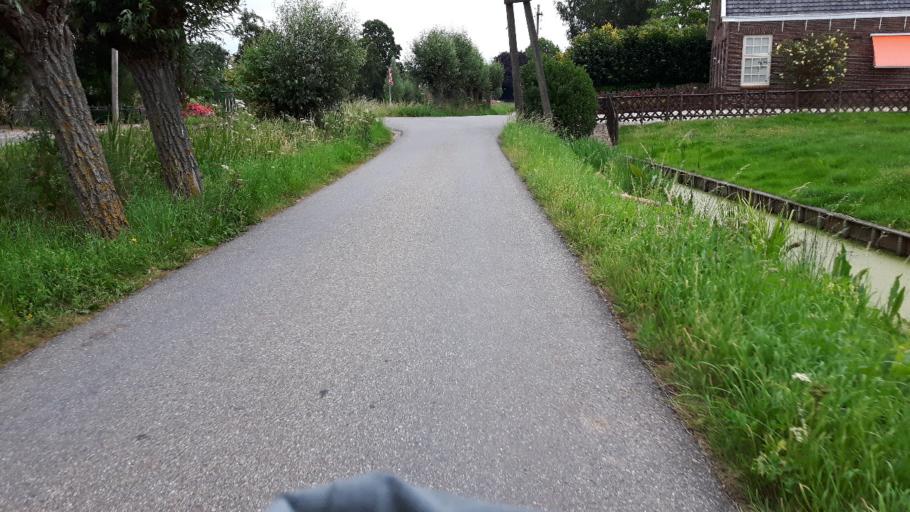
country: NL
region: South Holland
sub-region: Gemeente Vlist
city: Haastrecht
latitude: 51.9698
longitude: 4.7595
